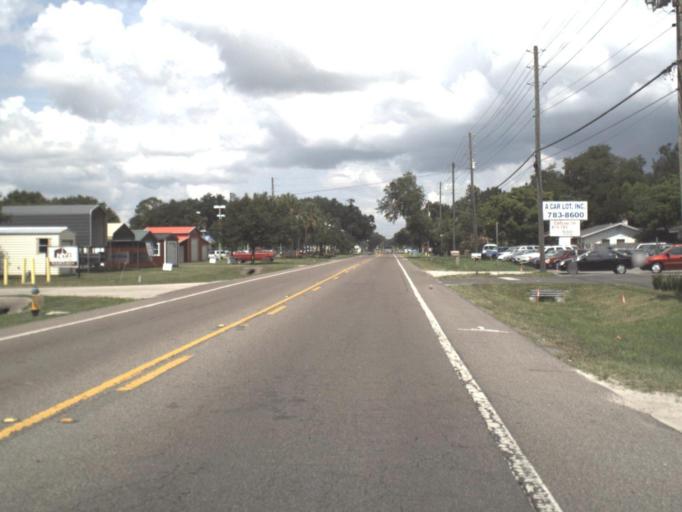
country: US
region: Florida
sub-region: Pasco County
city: Zephyrhills West
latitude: 28.2300
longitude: -82.2057
